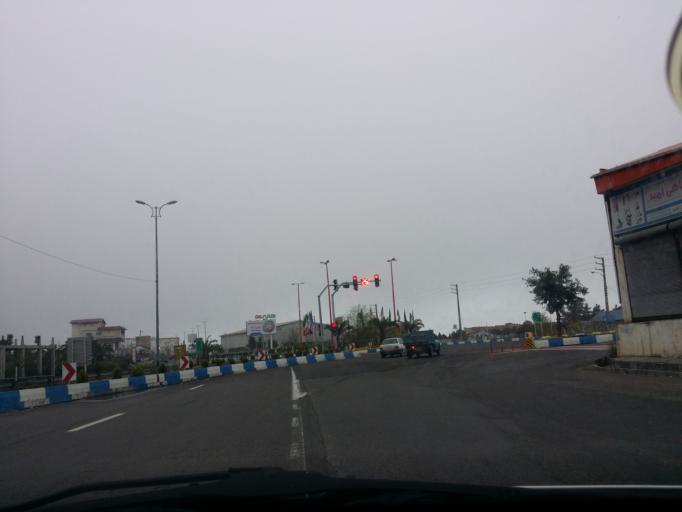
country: IR
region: Mazandaran
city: Tonekabon
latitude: 36.8385
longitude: 50.8341
